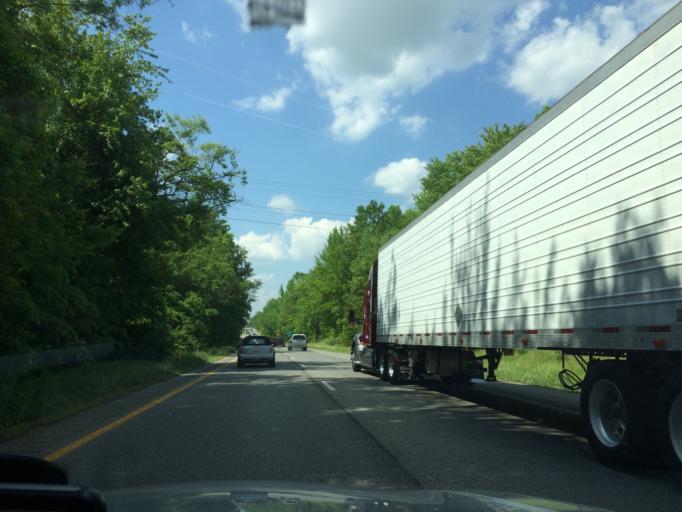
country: US
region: Maryland
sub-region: Prince George's County
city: Bowie
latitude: 38.9255
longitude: -76.7162
